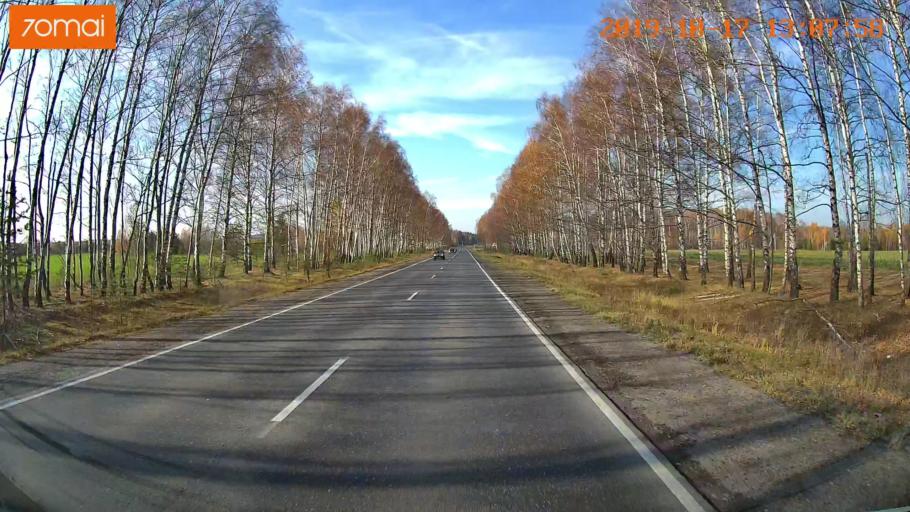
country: RU
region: Rjazan
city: Syntul
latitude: 54.9858
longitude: 41.2784
